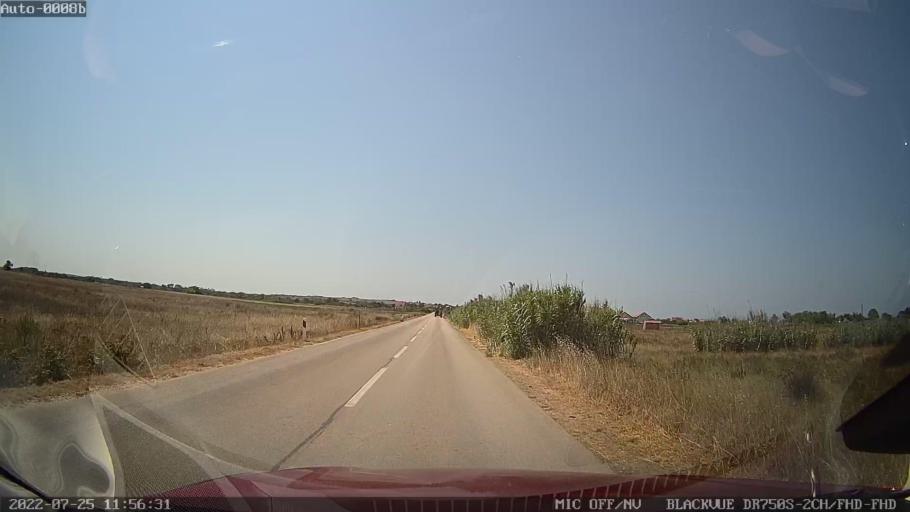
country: HR
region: Zadarska
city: Vrsi
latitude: 44.2491
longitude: 15.2176
